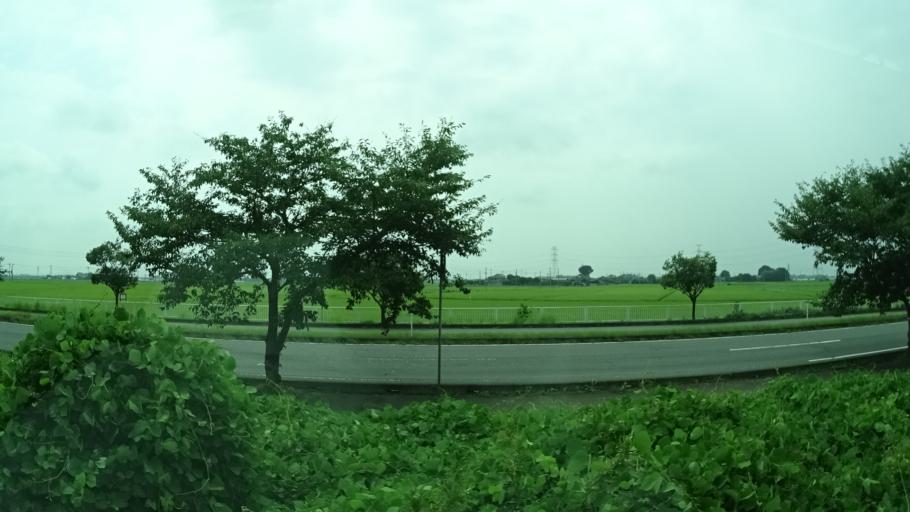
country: JP
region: Ibaraki
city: Shimodate
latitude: 36.3432
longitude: 139.9704
